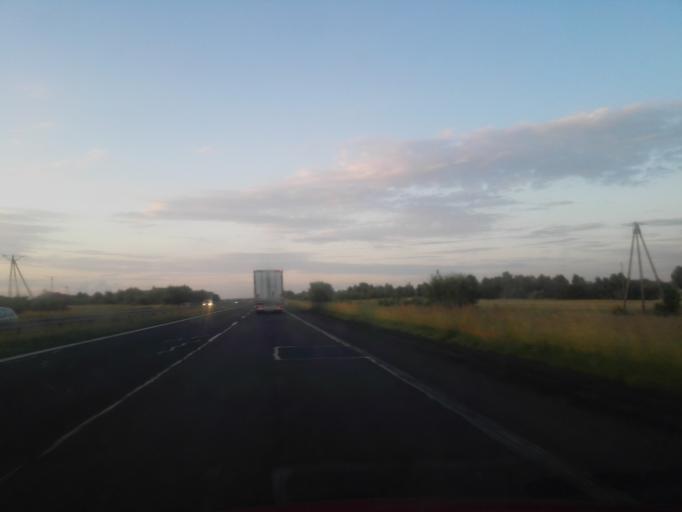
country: PL
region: Silesian Voivodeship
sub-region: Powiat czestochowski
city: Mykanow
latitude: 50.9184
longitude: 19.2191
